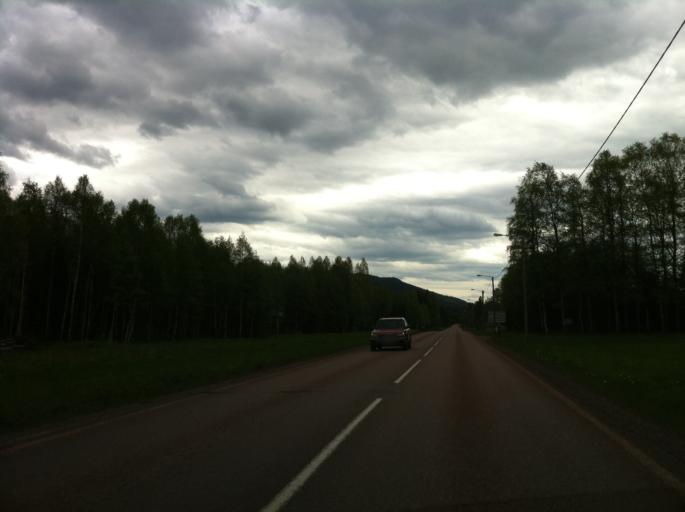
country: SE
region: Dalarna
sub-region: Malung-Saelens kommun
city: Malung
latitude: 61.0751
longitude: 13.3281
